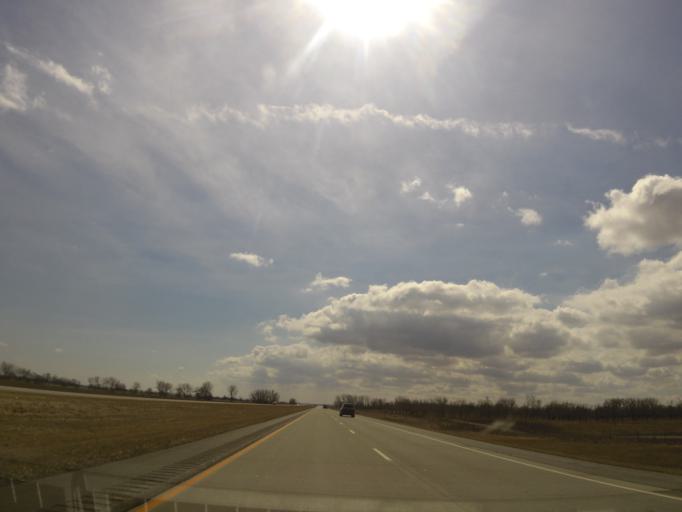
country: US
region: South Dakota
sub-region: Roberts County
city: Sisseton
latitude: 45.5054
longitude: -96.9896
